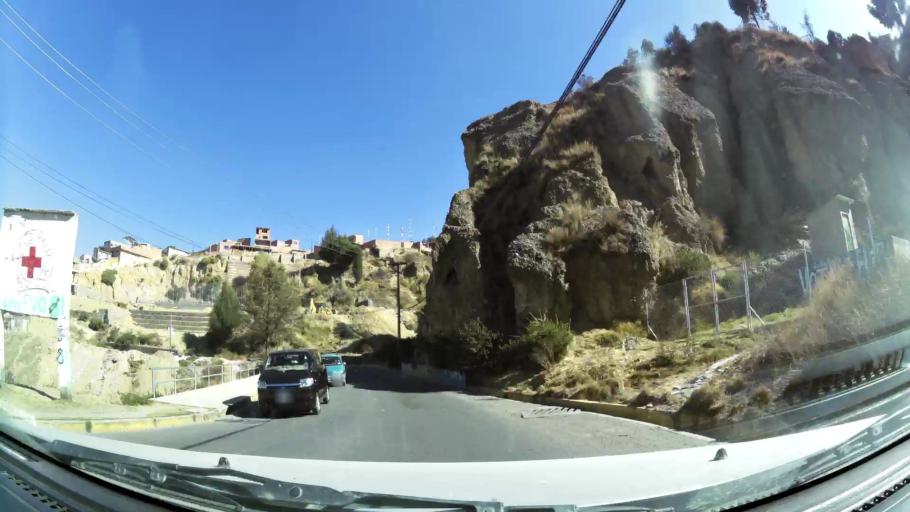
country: BO
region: La Paz
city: La Paz
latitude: -16.5201
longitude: -68.1431
